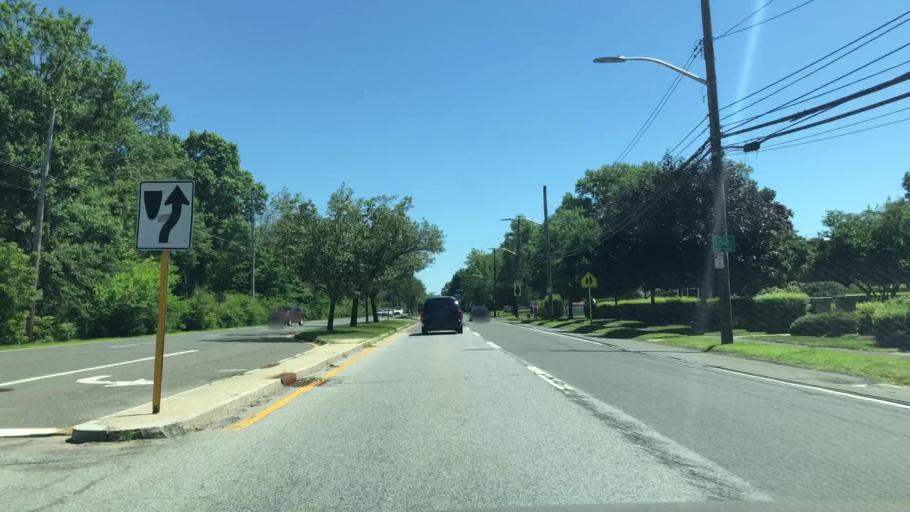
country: US
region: New York
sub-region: Westchester County
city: White Plains
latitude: 41.0102
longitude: -73.7532
